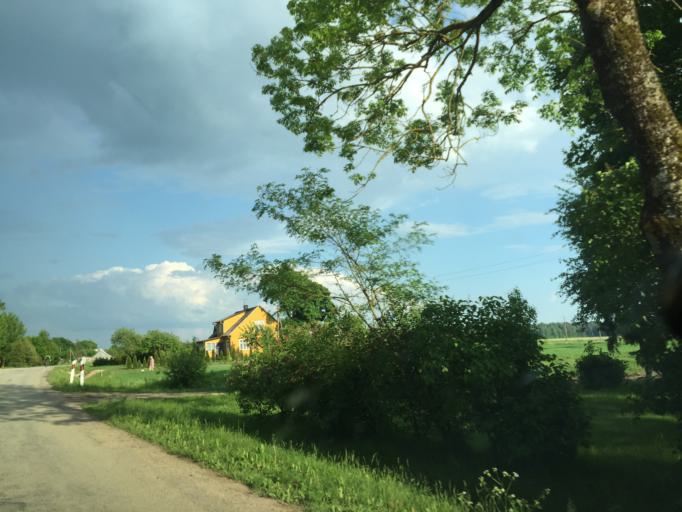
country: LT
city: Salantai
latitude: 56.0697
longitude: 21.4129
